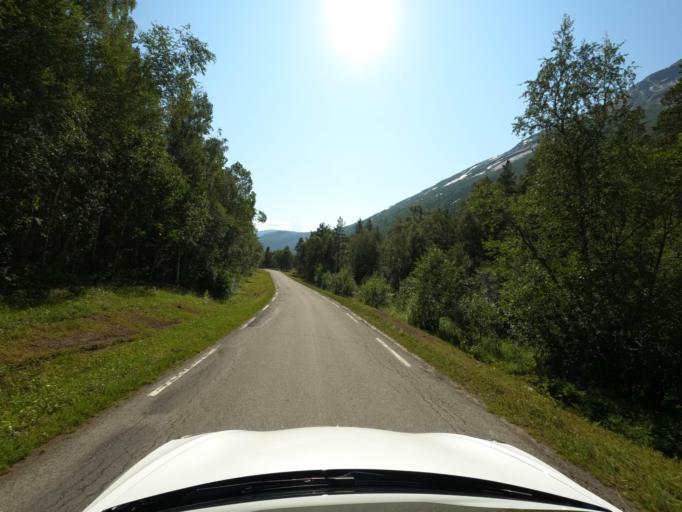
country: NO
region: Nordland
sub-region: Narvik
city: Narvik
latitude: 68.1902
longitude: 17.5524
